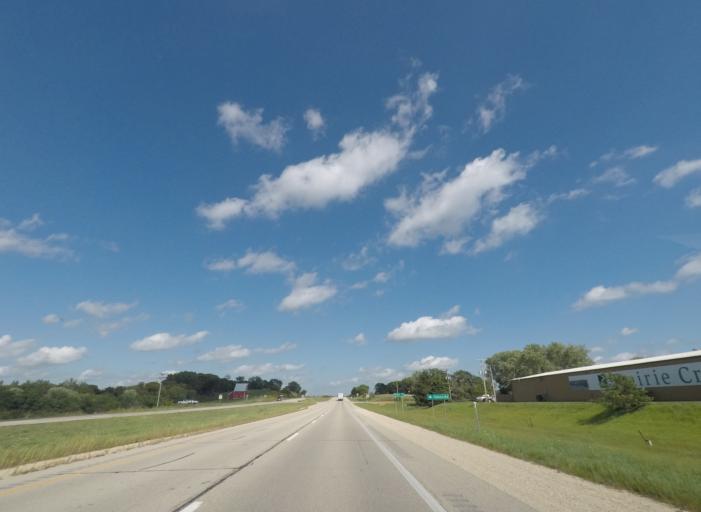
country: US
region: Iowa
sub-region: Dubuque County
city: Cascade
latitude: 42.3195
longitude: -90.9188
